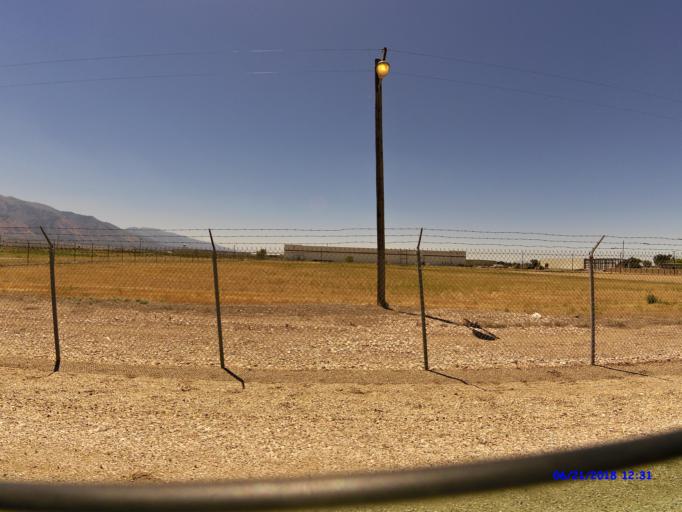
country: US
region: Utah
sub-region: Weber County
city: Harrisville
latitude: 41.2760
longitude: -112.0050
